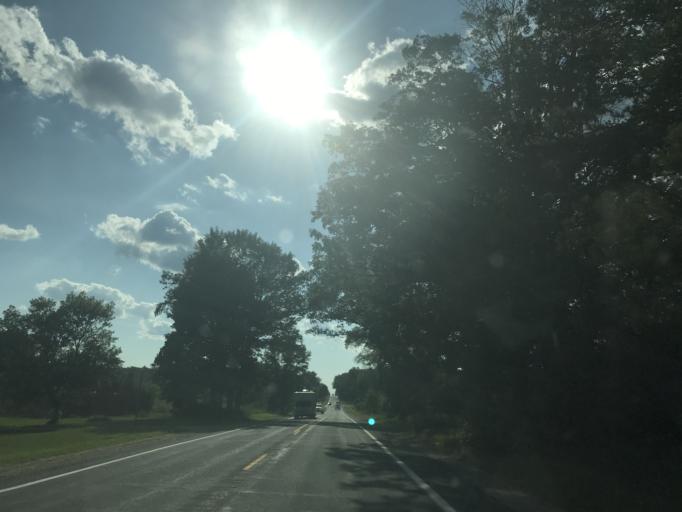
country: US
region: Michigan
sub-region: Newaygo County
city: White Cloud
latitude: 43.5684
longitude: -85.7875
